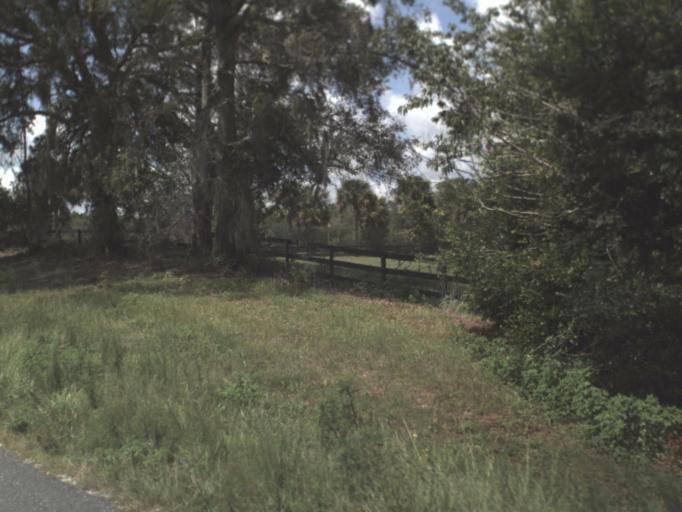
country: US
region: Florida
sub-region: Gilchrist County
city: Trenton
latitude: 29.8287
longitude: -82.8673
